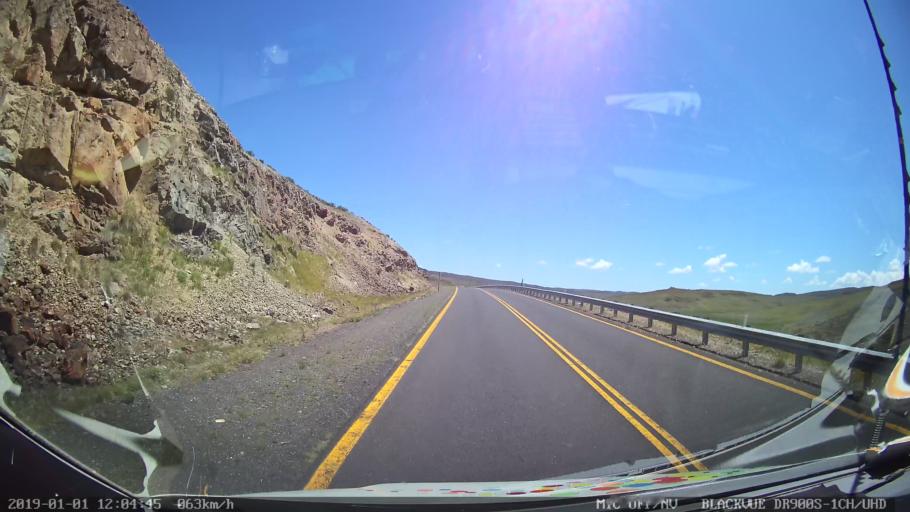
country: AU
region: New South Wales
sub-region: Snowy River
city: Jindabyne
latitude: -35.8643
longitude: 148.4961
